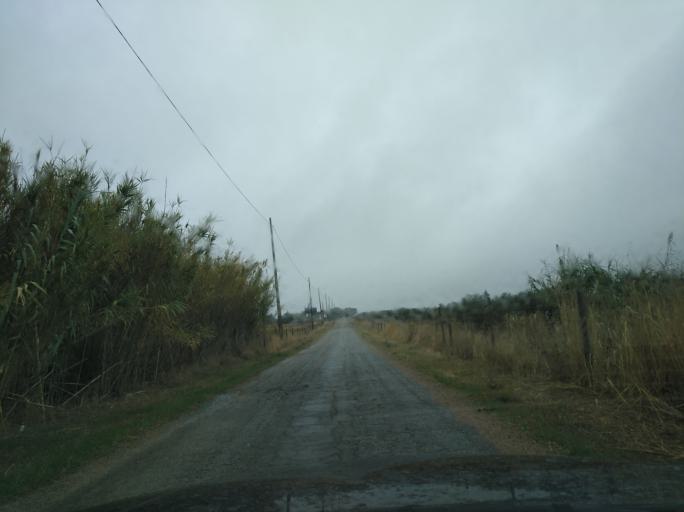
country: PT
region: Portalegre
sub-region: Campo Maior
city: Campo Maior
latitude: 38.9736
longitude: -7.0719
